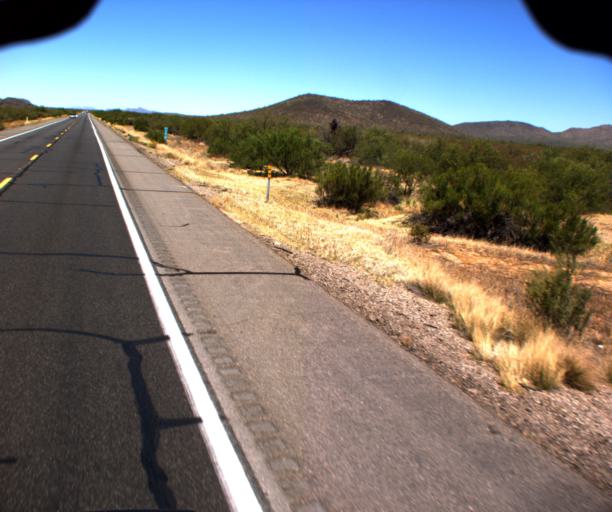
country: US
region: Arizona
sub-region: Yavapai County
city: Congress
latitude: 34.1595
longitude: -113.0024
